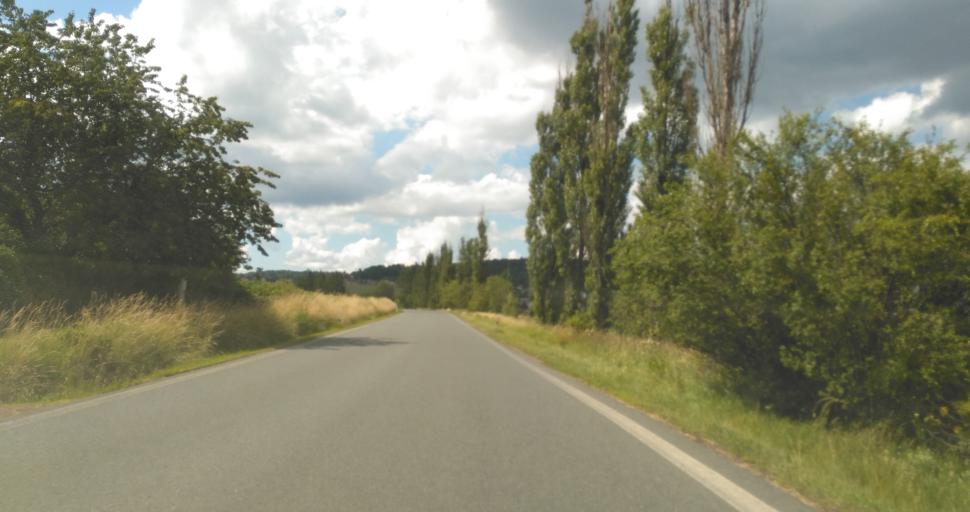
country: CZ
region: Plzensky
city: Zbiroh
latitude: 49.8454
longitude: 13.7738
